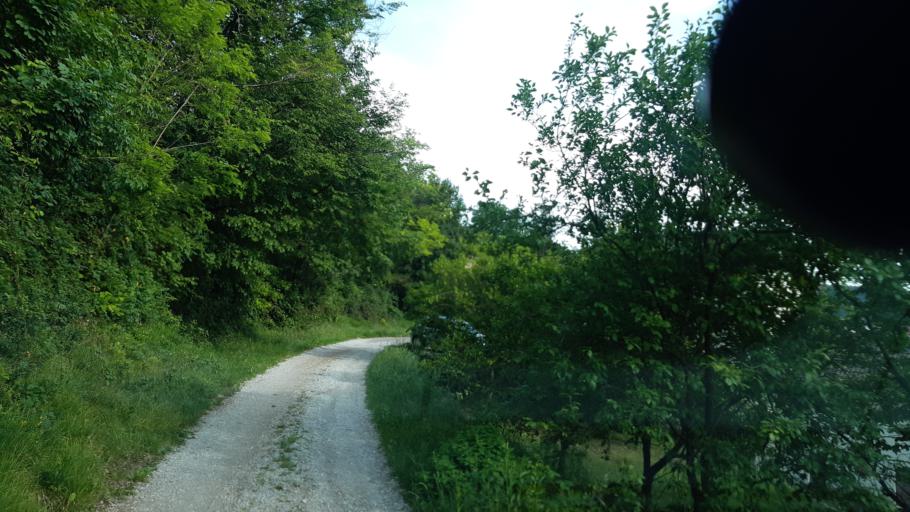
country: SI
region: Ajdovscina
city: Lokavec
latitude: 45.8186
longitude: 13.8515
